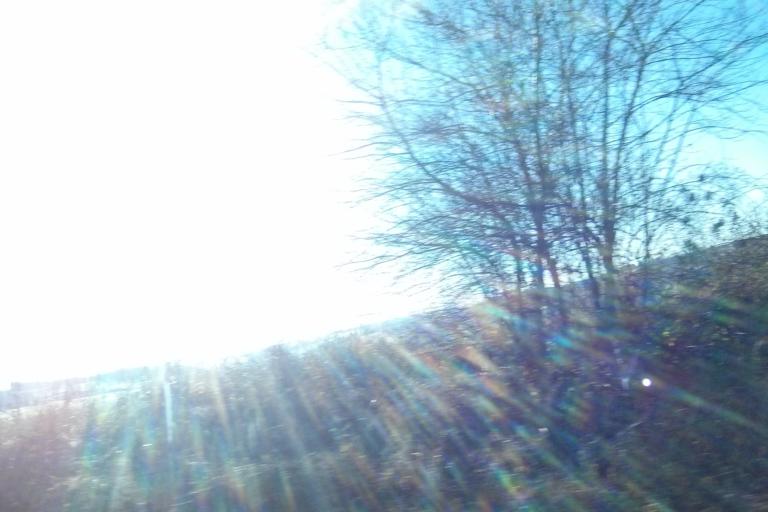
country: DE
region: North Rhine-Westphalia
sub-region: Regierungsbezirk Koln
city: Hennef
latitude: 50.7660
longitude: 7.3142
